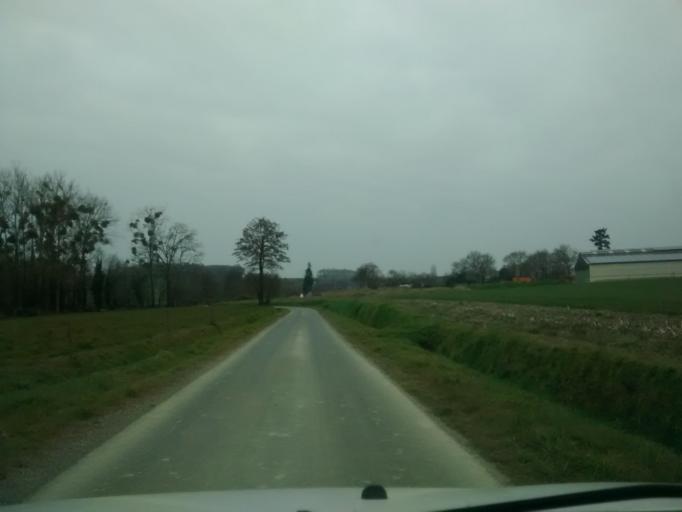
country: FR
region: Brittany
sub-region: Departement d'Ille-et-Vilaine
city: Bazouges-la-Perouse
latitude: 48.3856
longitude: -1.5556
